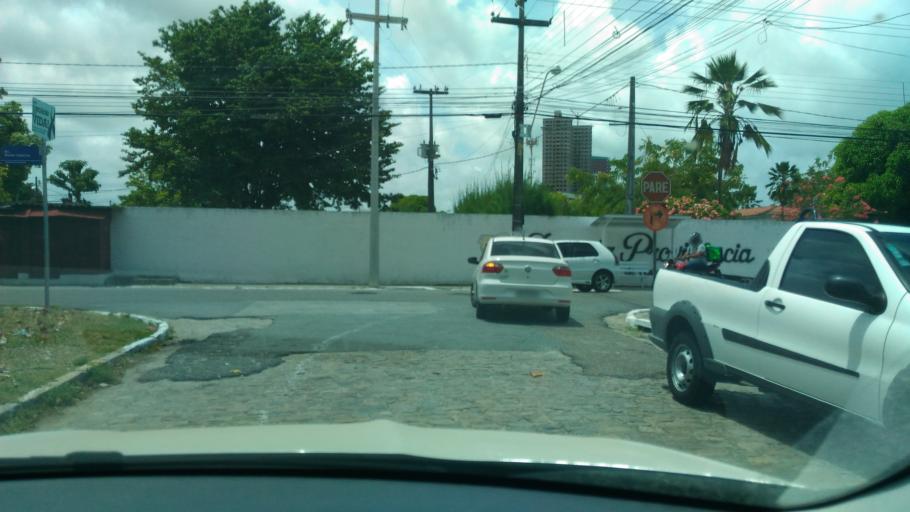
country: BR
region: Paraiba
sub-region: Joao Pessoa
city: Joao Pessoa
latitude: -7.1167
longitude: -34.8608
